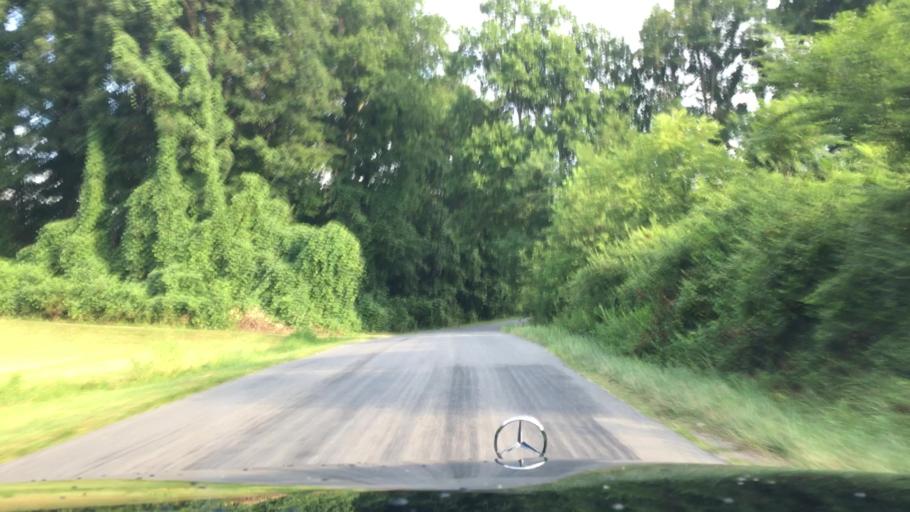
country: US
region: Virginia
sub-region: Campbell County
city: Timberlake
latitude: 37.2344
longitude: -79.2903
